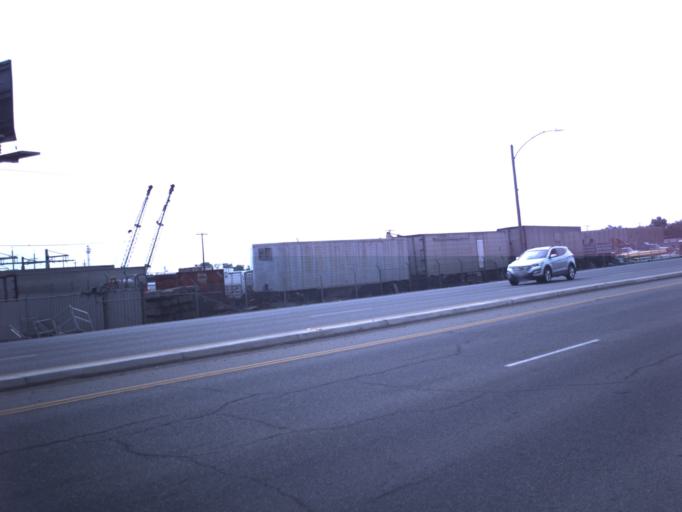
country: US
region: Utah
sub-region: Salt Lake County
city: Salt Lake City
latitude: 40.7979
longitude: -111.9078
